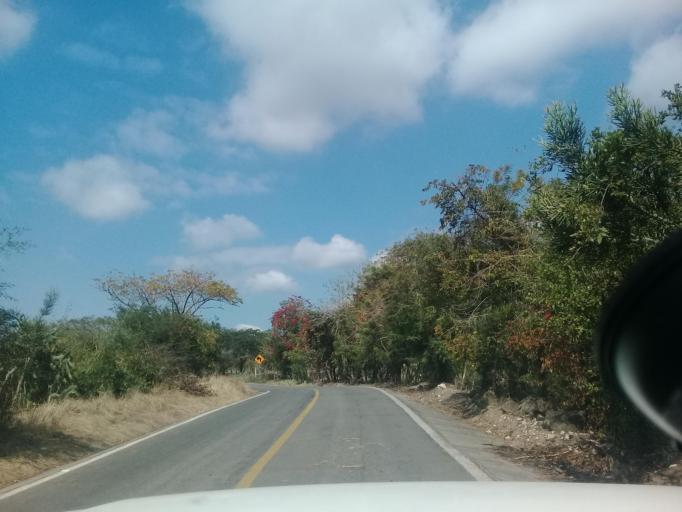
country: MX
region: Veracruz
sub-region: Coatepec
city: Tuzamapan
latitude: 19.4166
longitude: -96.8522
